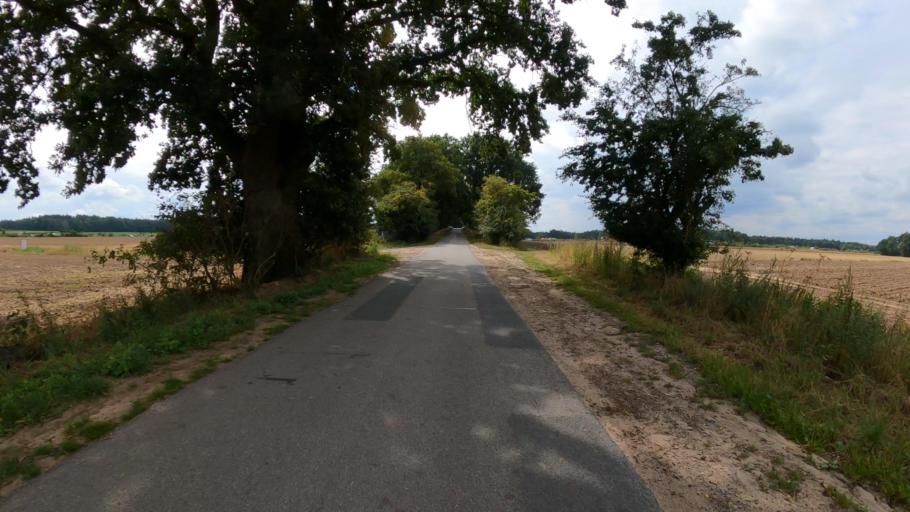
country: DE
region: Lower Saxony
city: Appel
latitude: 53.3719
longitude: 9.7572
